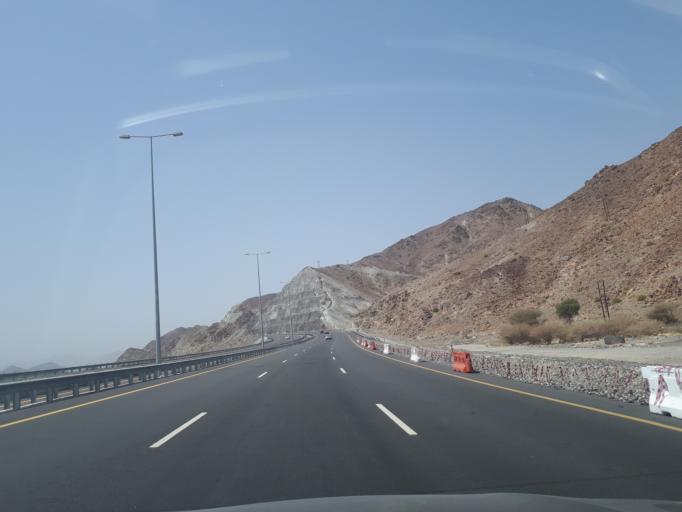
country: OM
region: Muhafazat ad Dakhiliyah
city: Bidbid
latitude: 23.3764
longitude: 58.1033
